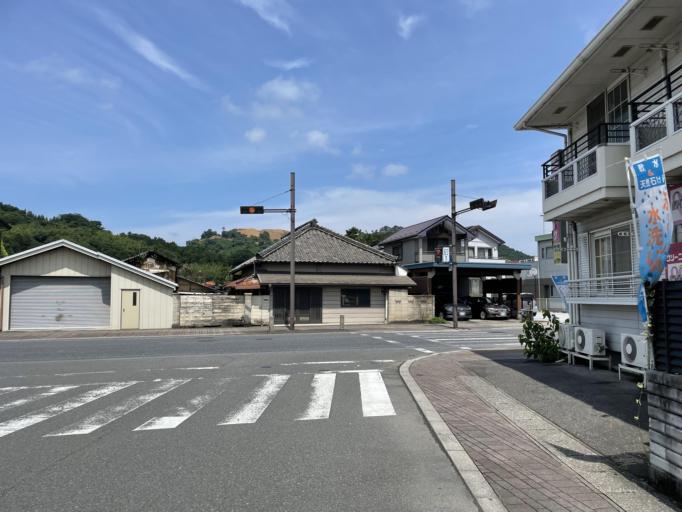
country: JP
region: Tochigi
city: Tanuma
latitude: 36.3987
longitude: 139.6080
